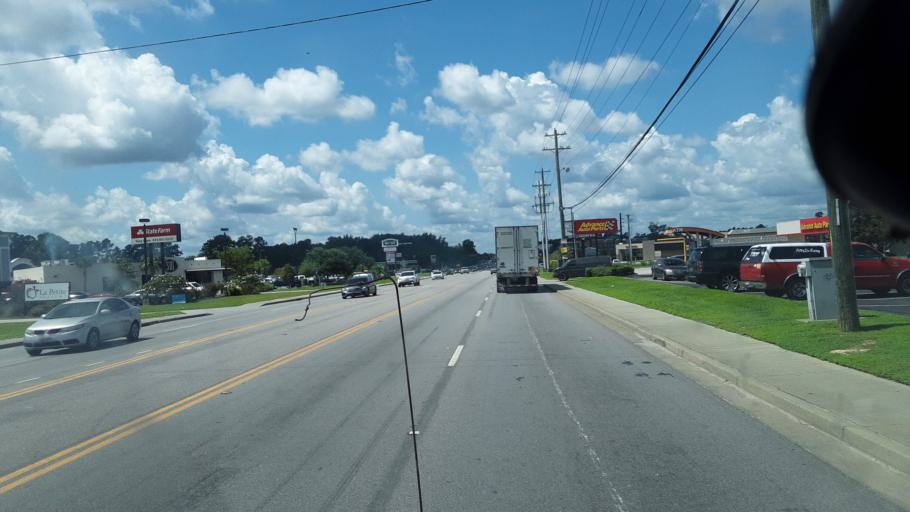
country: US
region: South Carolina
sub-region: Berkeley County
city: Sangaree
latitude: 33.0409
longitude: -80.1355
